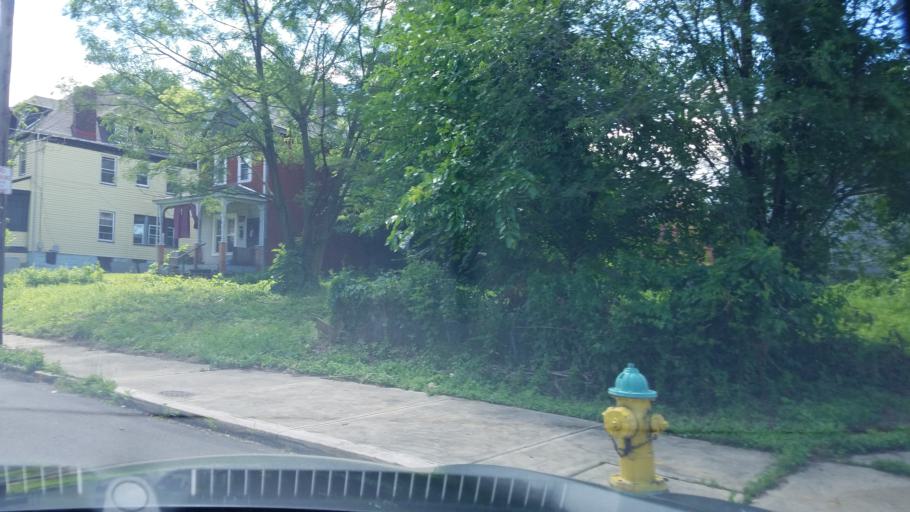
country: US
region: Pennsylvania
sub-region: Allegheny County
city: Edgewood
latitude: 40.4362
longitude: -79.8826
